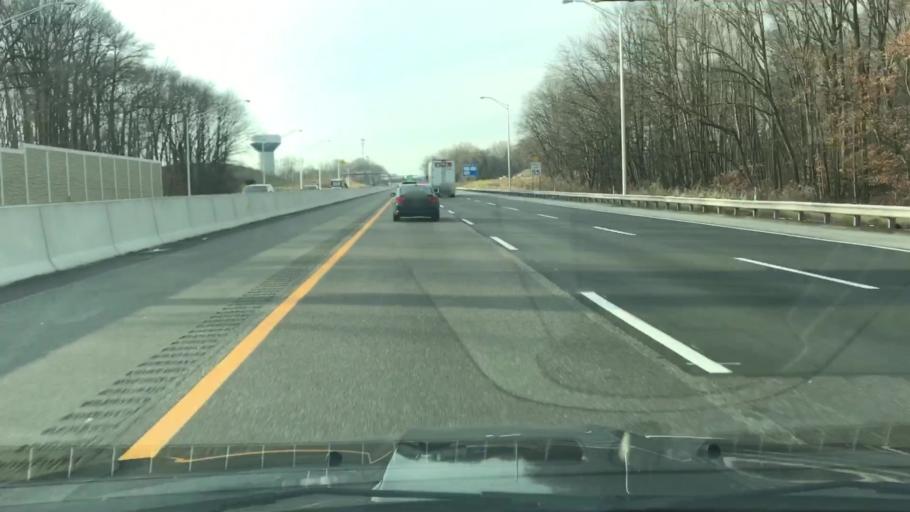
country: US
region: Pennsylvania
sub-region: Bucks County
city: Trevose
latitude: 40.1289
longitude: -74.9568
